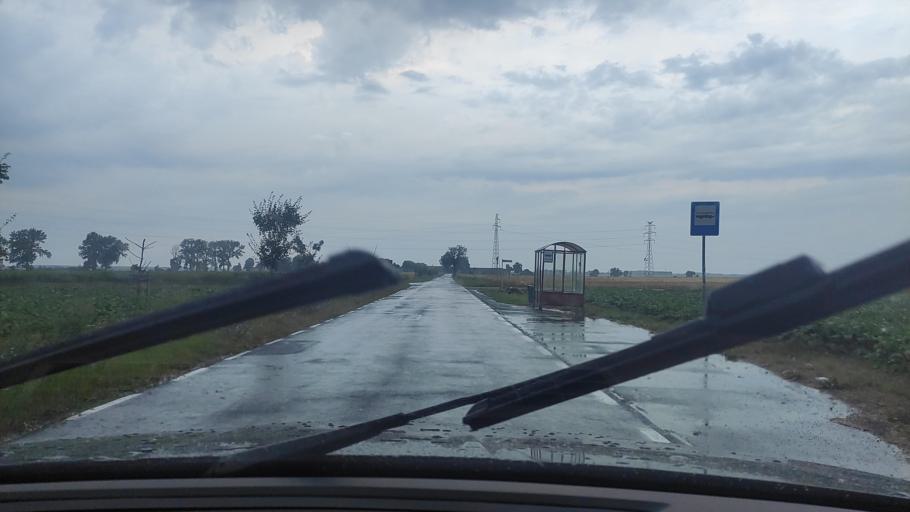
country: PL
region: Greater Poland Voivodeship
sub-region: Powiat poznanski
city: Kleszczewo
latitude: 52.2920
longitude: 17.1727
